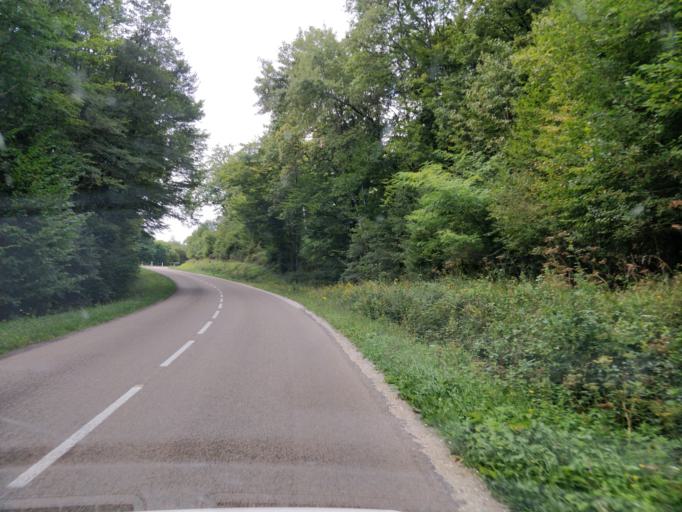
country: FR
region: Bourgogne
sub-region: Departement de l'Yonne
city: Saint-Florentin
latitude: 48.0985
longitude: 3.6807
